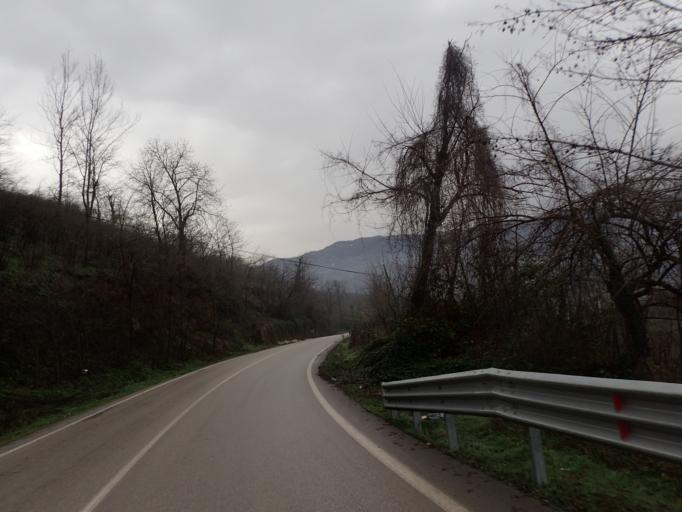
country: TR
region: Ordu
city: Camas
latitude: 40.9301
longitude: 37.5064
